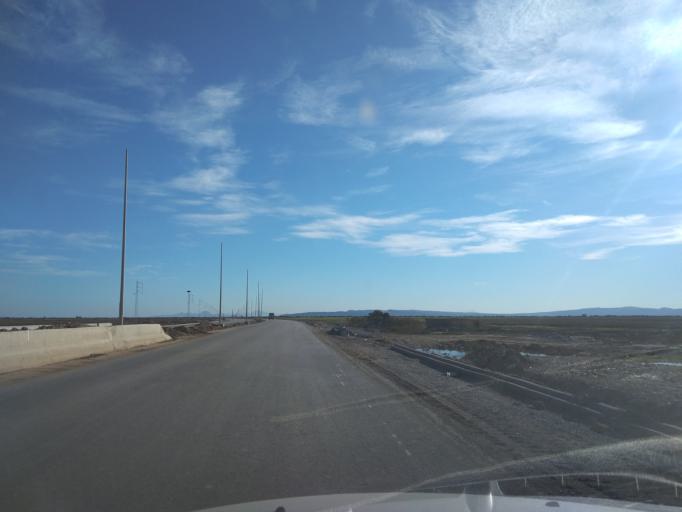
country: TN
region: Ariana
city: Qal'at al Andalus
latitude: 37.0381
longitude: 10.1325
